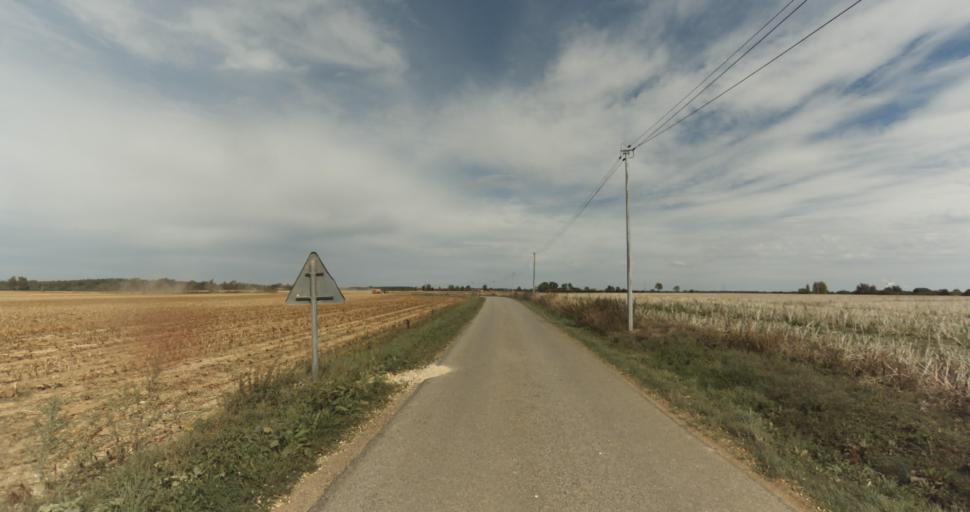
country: FR
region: Lower Normandy
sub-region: Departement du Calvados
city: Orbec
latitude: 48.9501
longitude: 0.3986
